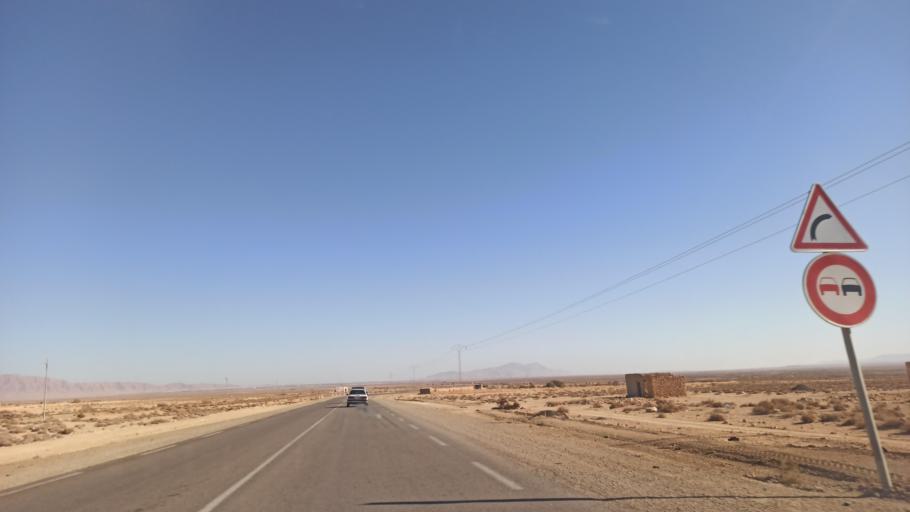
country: TN
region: Gafsa
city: Al Metlaoui
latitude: 34.3309
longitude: 8.5542
